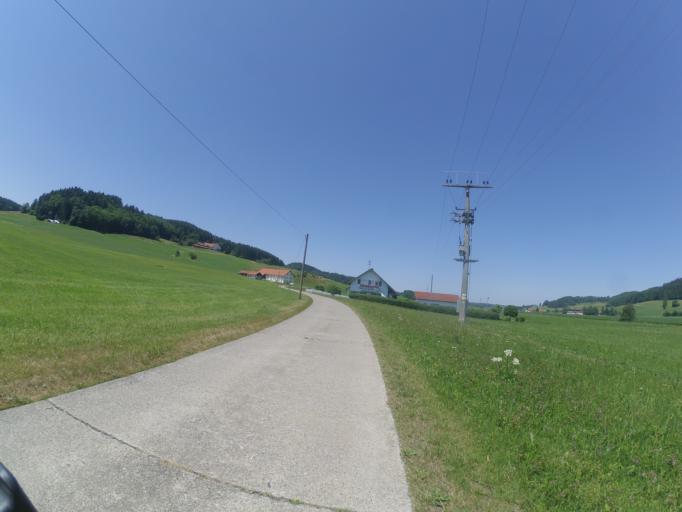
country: DE
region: Bavaria
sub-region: Swabia
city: Bohen
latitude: 47.8669
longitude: 10.3427
